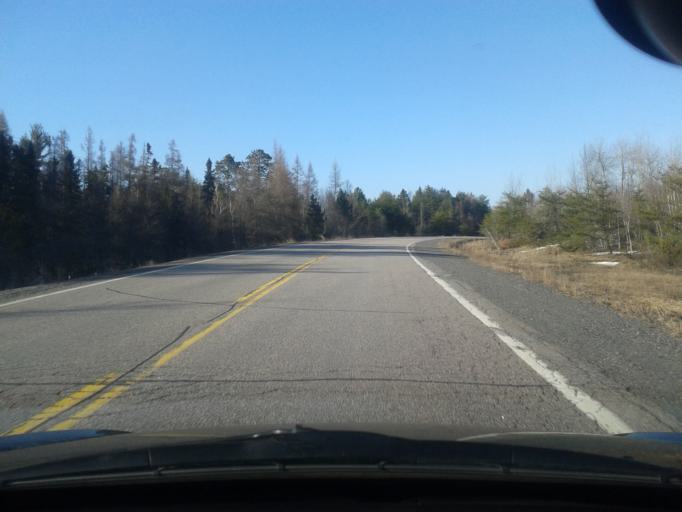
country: CA
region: Ontario
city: Greater Sudbury
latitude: 46.2628
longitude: -80.3047
